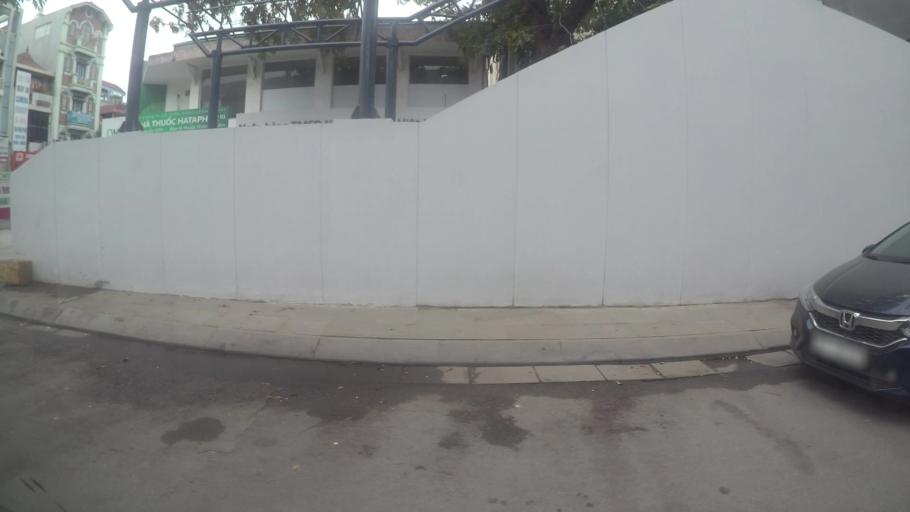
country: VN
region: Ha Noi
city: Ha Dong
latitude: 20.9698
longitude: 105.7744
